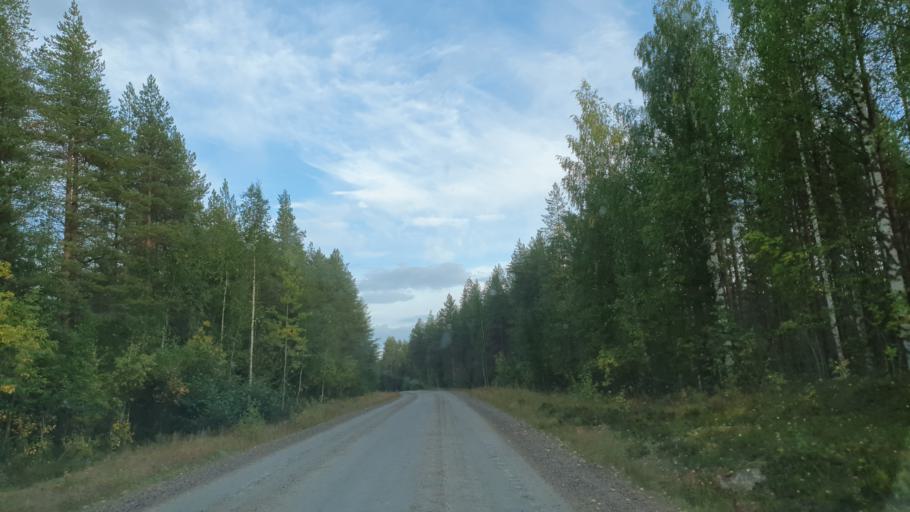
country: FI
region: Kainuu
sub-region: Kehys-Kainuu
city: Kuhmo
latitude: 64.4144
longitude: 29.5243
